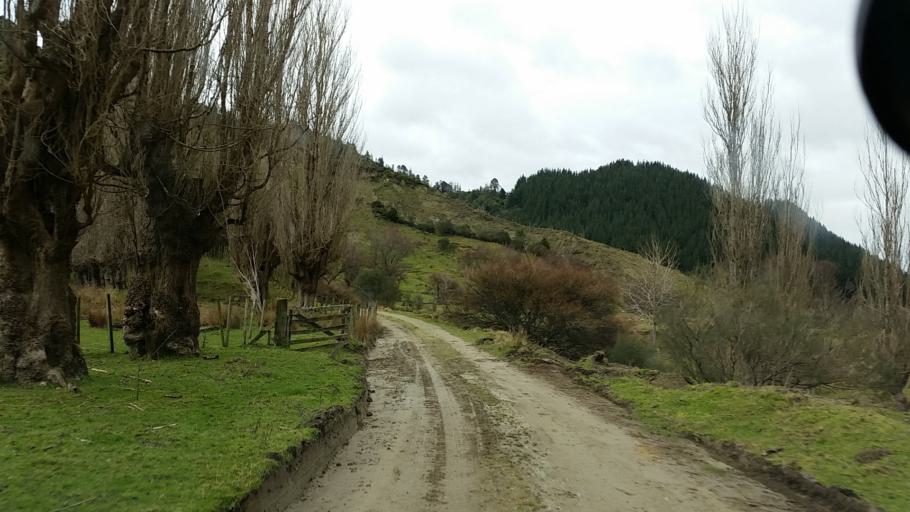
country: NZ
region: Taranaki
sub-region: South Taranaki District
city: Patea
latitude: -39.6548
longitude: 174.7515
